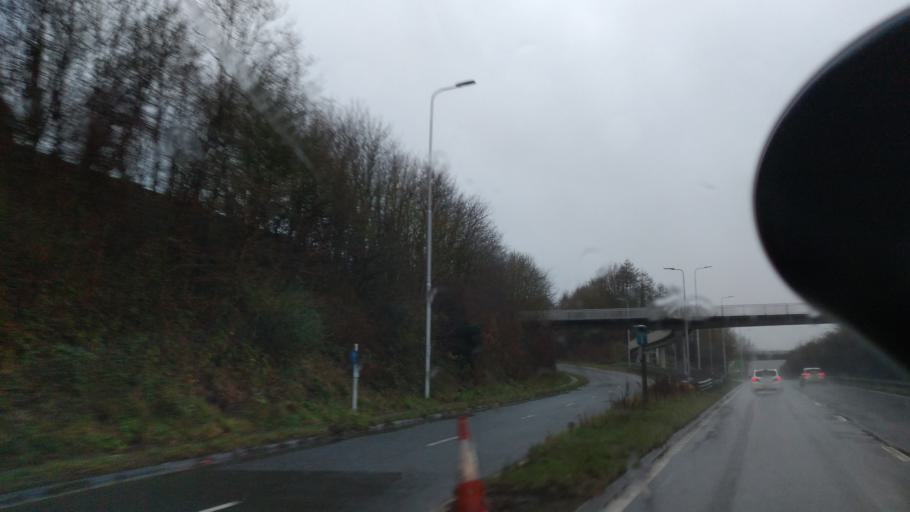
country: GB
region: England
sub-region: Brighton and Hove
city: Rottingdean
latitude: 50.8635
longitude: -0.0772
